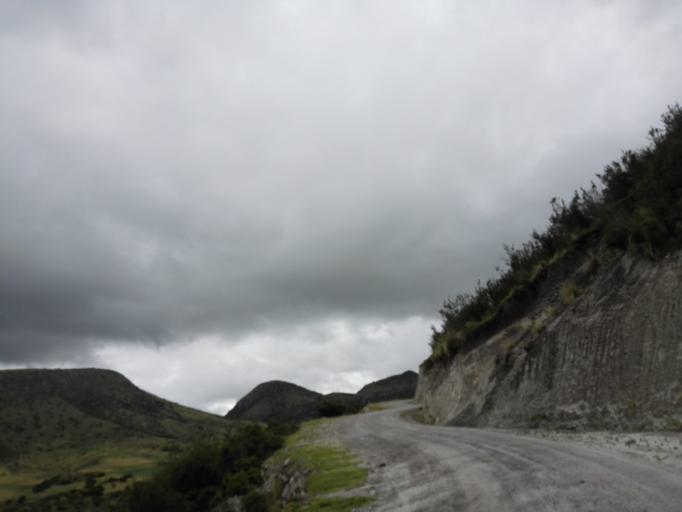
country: PE
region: Ayacucho
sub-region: Provincia de Huamanga
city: Vinchos
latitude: -13.3207
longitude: -74.4445
